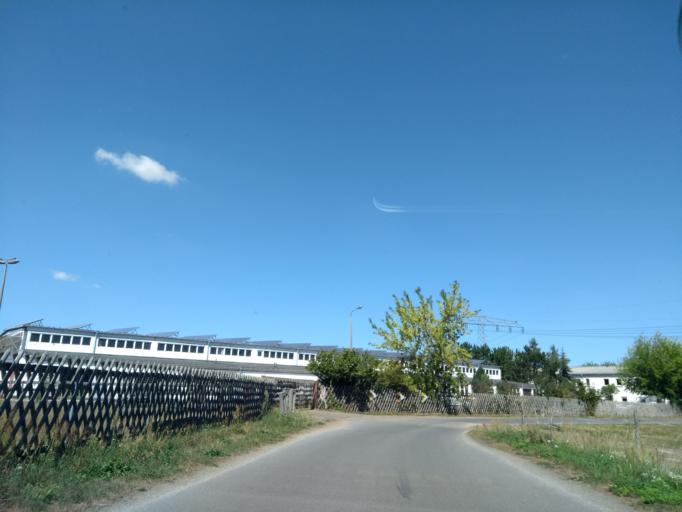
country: DE
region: Brandenburg
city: Lubbenau
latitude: 51.8335
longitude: 13.9502
